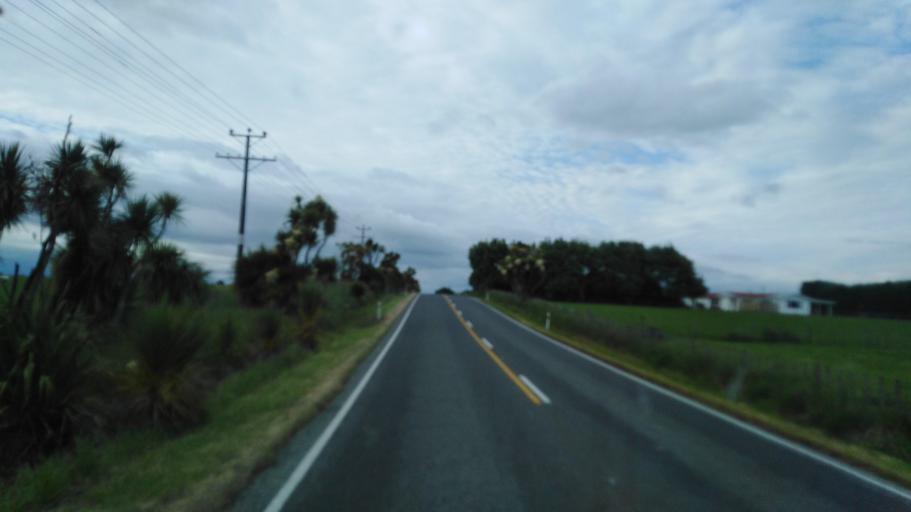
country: NZ
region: Manawatu-Wanganui
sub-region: Rangitikei District
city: Bulls
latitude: -40.1154
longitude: 175.3573
